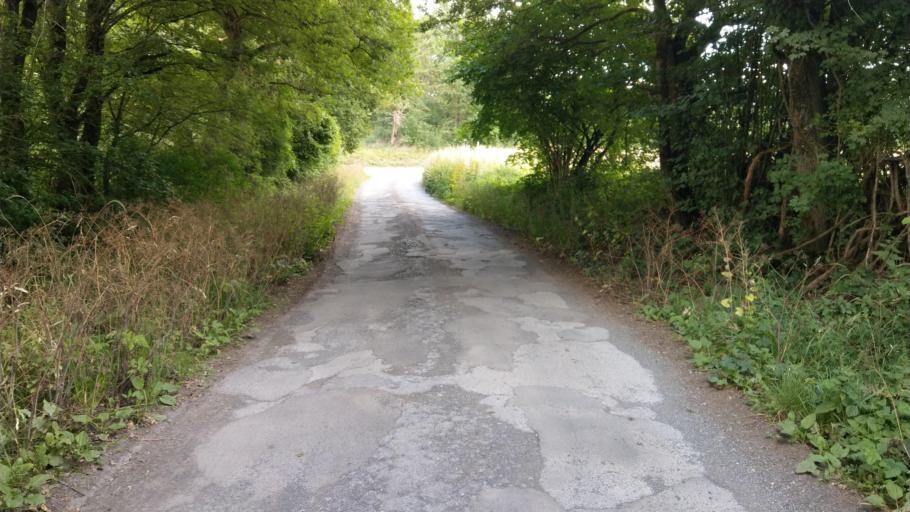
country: BE
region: Wallonia
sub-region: Province de Namur
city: Couvin
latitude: 50.0634
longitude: 4.4285
